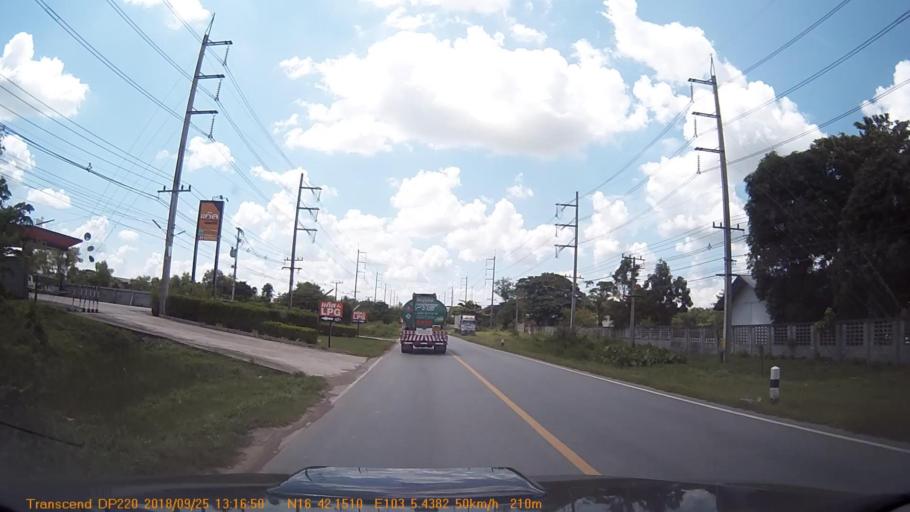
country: TH
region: Khon Kaen
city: Kranuan
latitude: 16.7025
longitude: 103.0908
